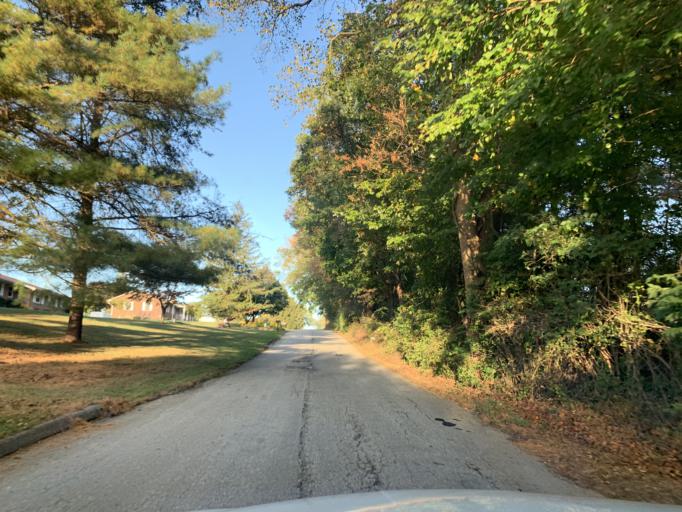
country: US
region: Maryland
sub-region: Harford County
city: Fallston
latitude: 39.4867
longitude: -76.4466
